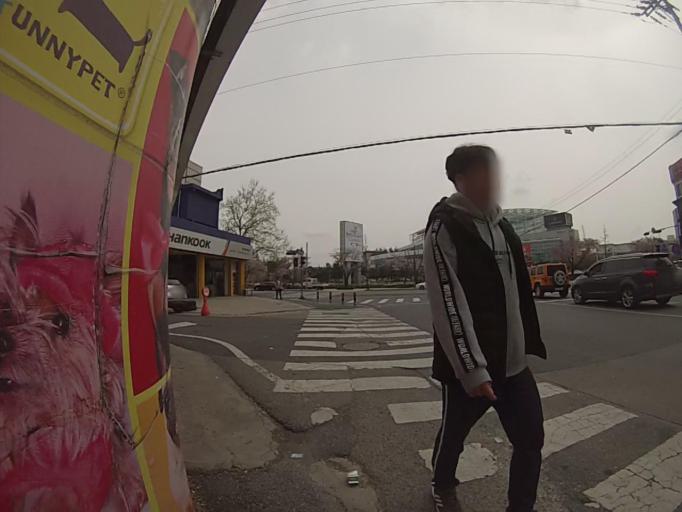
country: KR
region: Daejeon
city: Songgang-dong
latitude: 36.3631
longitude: 127.3558
